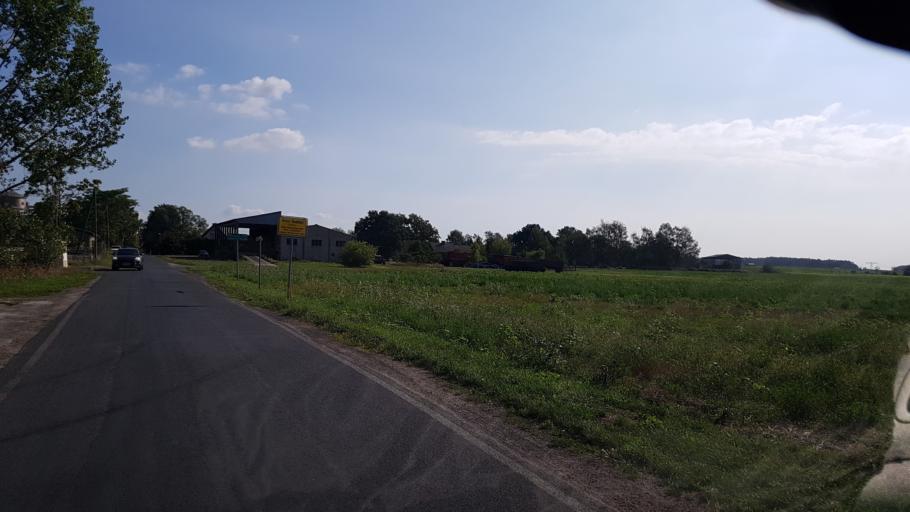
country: DE
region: Brandenburg
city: Luebben
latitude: 51.8687
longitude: 13.8760
